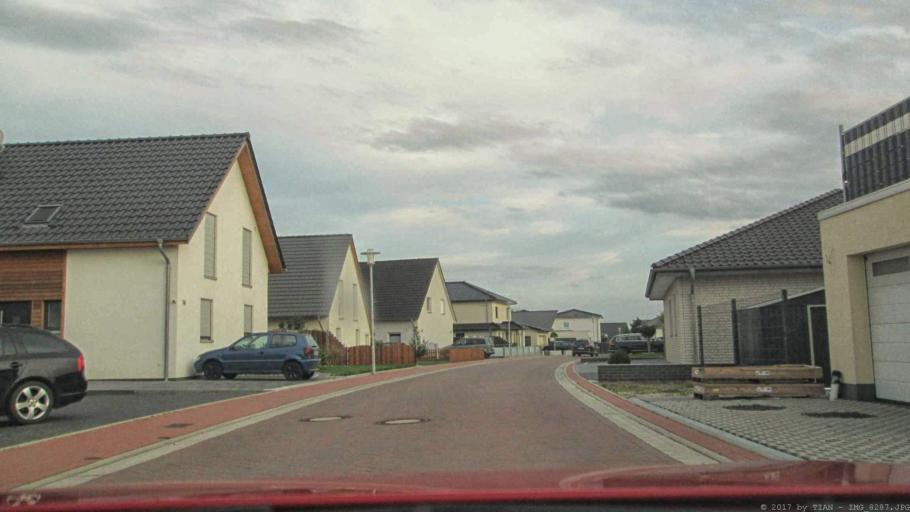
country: DE
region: Lower Saxony
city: Weyhausen
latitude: 52.4000
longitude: 10.7236
